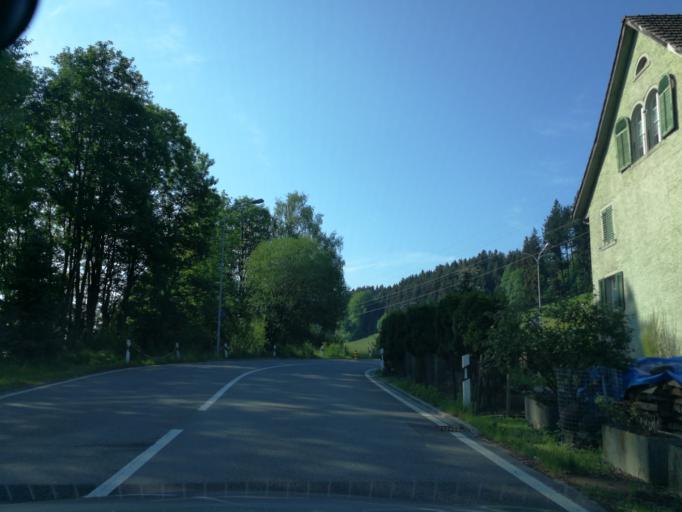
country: CH
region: Zurich
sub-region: Bezirk Horgen
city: Horgen / Allmend
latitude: 47.2301
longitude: 8.6145
